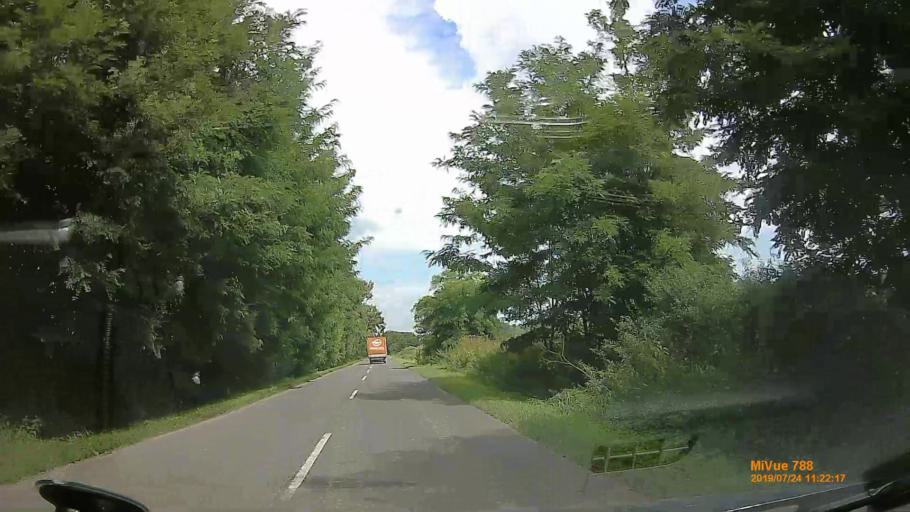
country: HU
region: Szabolcs-Szatmar-Bereg
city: Tarpa
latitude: 48.1745
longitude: 22.4623
